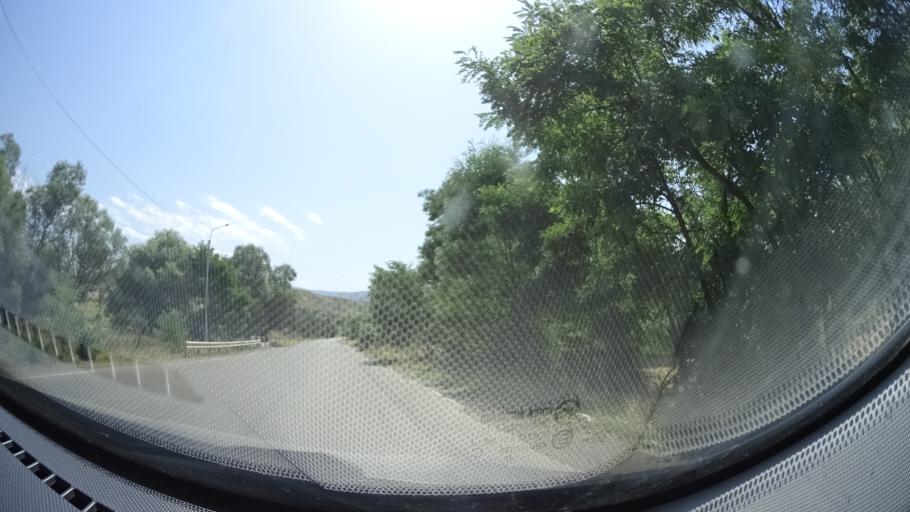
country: GE
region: Samtskhe-Javakheti
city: Aspindza
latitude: 41.5883
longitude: 43.2337
